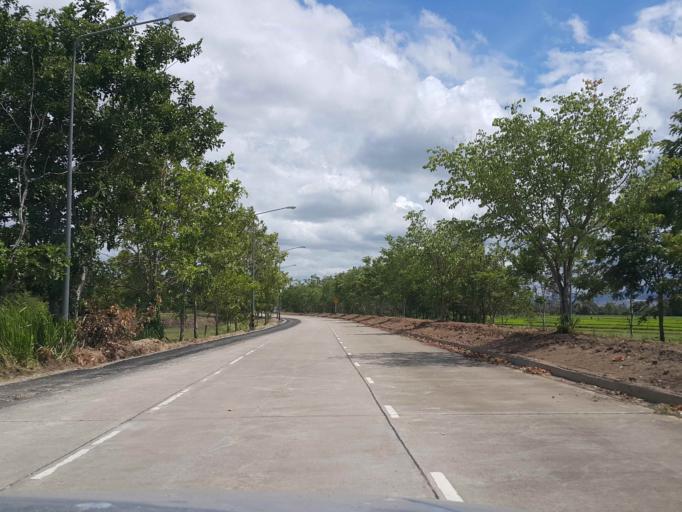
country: TH
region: Tak
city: Tak
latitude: 16.8631
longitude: 99.1142
